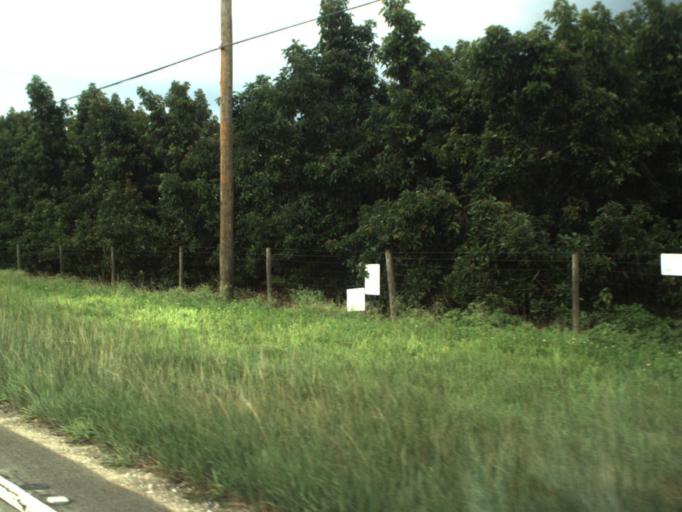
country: US
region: Florida
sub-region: Miami-Dade County
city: Richmond West
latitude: 25.5610
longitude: -80.4782
